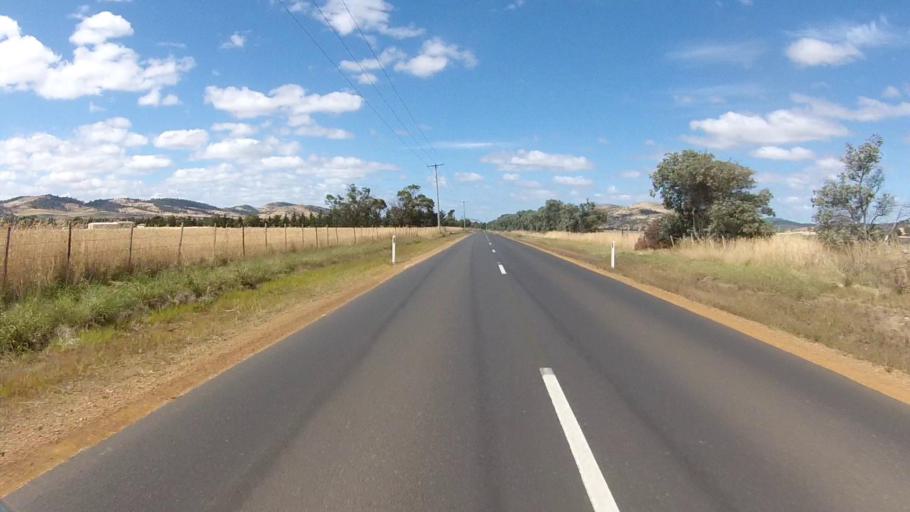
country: AU
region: Tasmania
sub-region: Clarence
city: Cambridge
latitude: -42.7134
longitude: 147.4307
